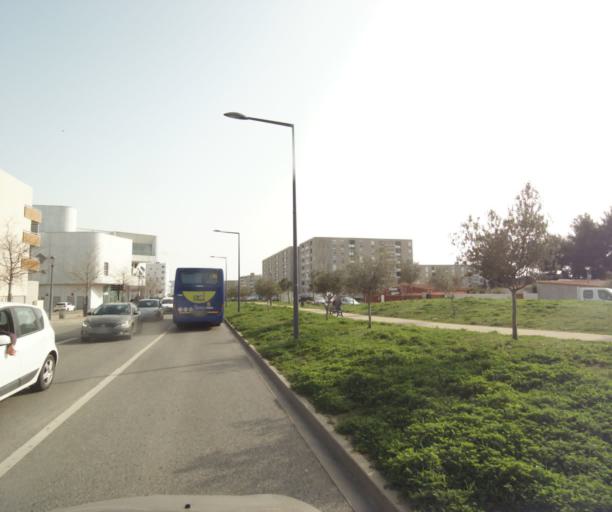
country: FR
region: Provence-Alpes-Cote d'Azur
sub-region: Departement des Bouches-du-Rhone
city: Vitrolles
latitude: 43.4439
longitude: 5.2517
